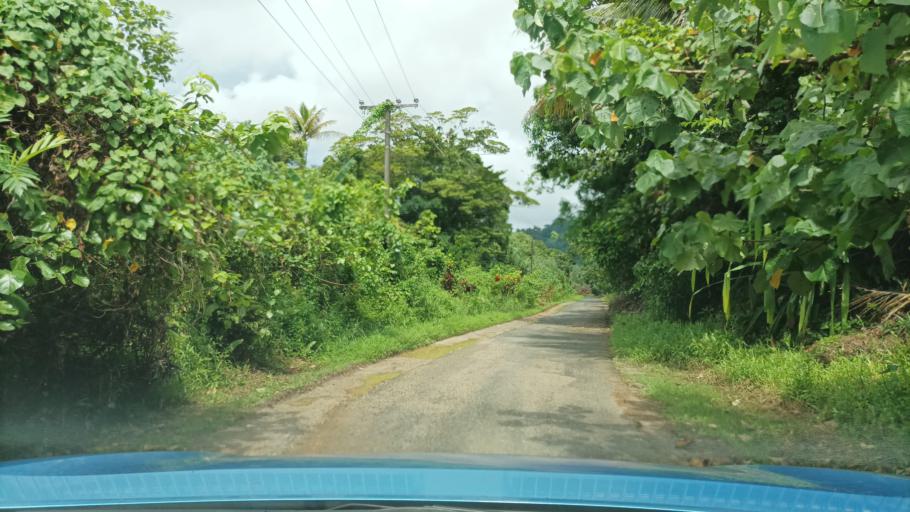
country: FM
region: Pohnpei
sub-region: Madolenihm Municipality
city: Madolenihm Municipality Government
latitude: 6.8867
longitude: 158.3163
